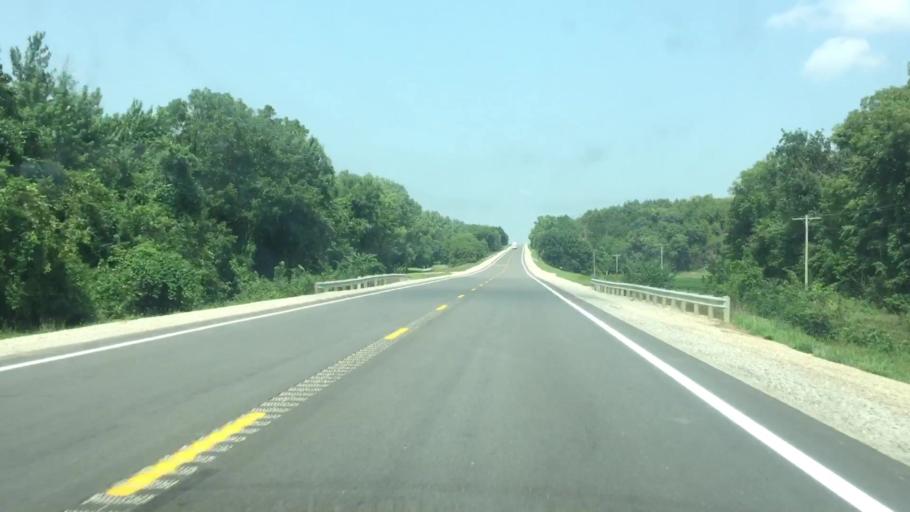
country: US
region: Kansas
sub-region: Anderson County
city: Garnett
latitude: 38.3400
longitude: -95.2488
